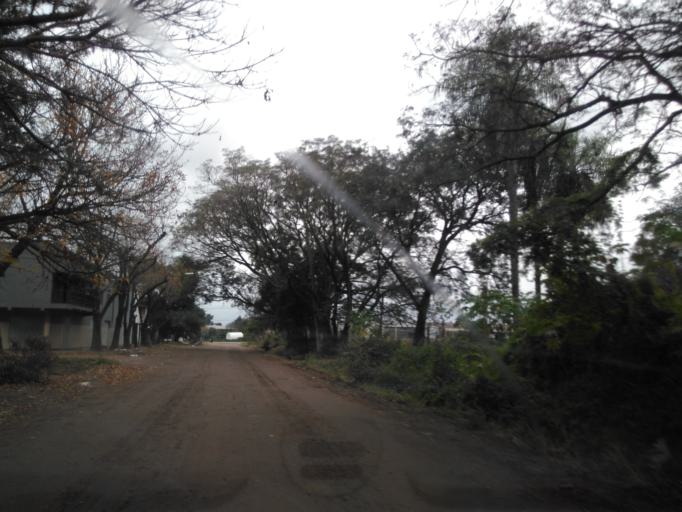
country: AR
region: Chaco
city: Fontana
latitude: -27.4292
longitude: -59.0140
